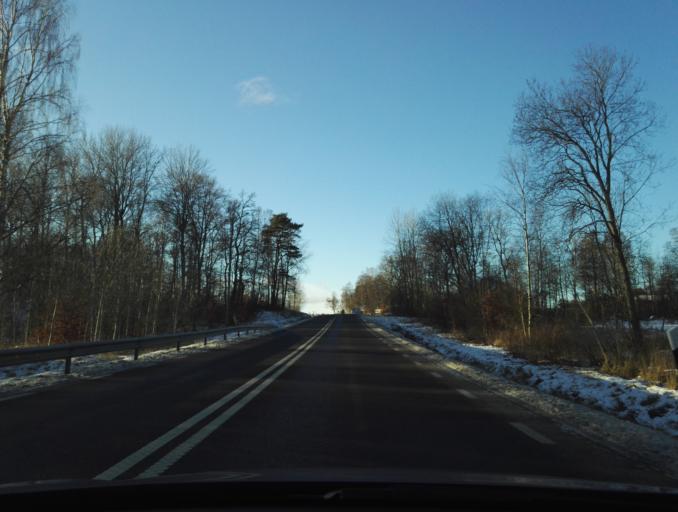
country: SE
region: Kronoberg
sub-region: Vaxjo Kommun
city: Vaexjoe
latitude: 56.8526
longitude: 14.7266
